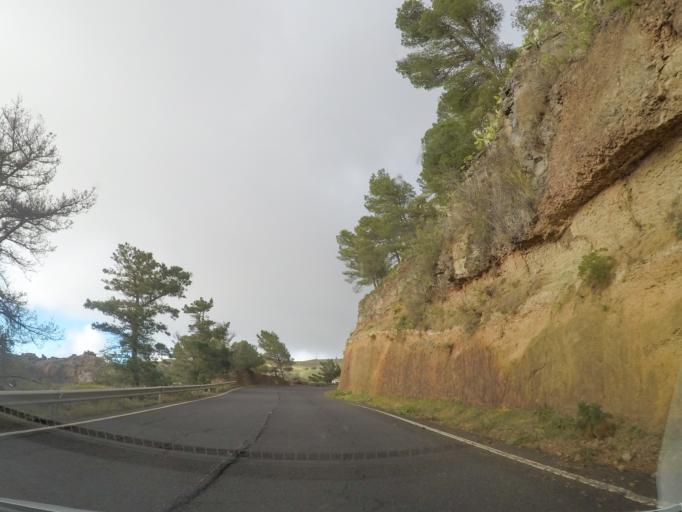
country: ES
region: Canary Islands
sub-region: Provincia de Santa Cruz de Tenerife
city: Vallehermosa
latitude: 28.1281
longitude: -17.3216
